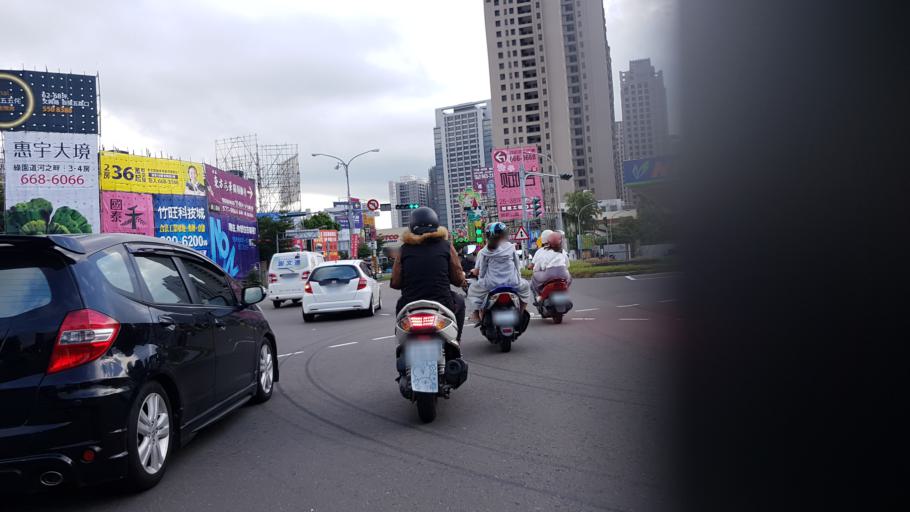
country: TW
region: Taiwan
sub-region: Hsinchu
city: Zhubei
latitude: 24.7960
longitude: 121.0132
